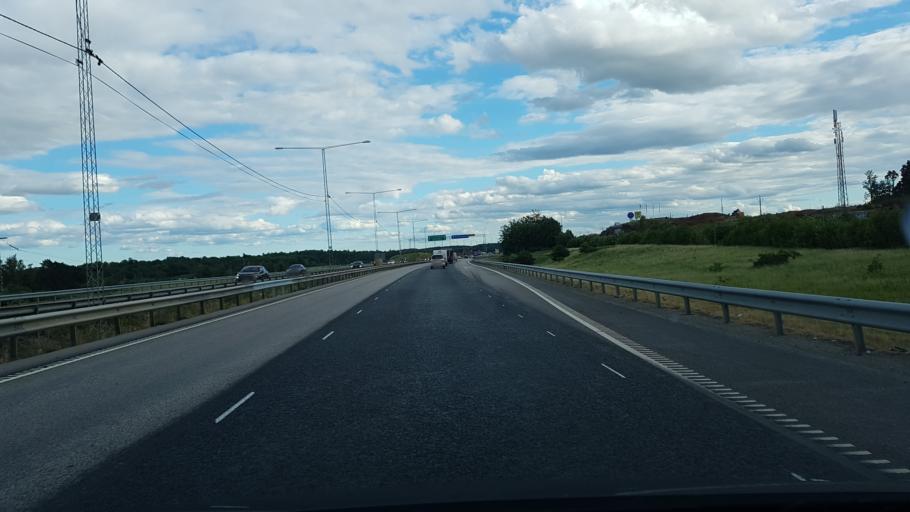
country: SE
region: Stockholm
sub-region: Sigtuna Kommun
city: Rosersberg
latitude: 59.5808
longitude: 17.9002
